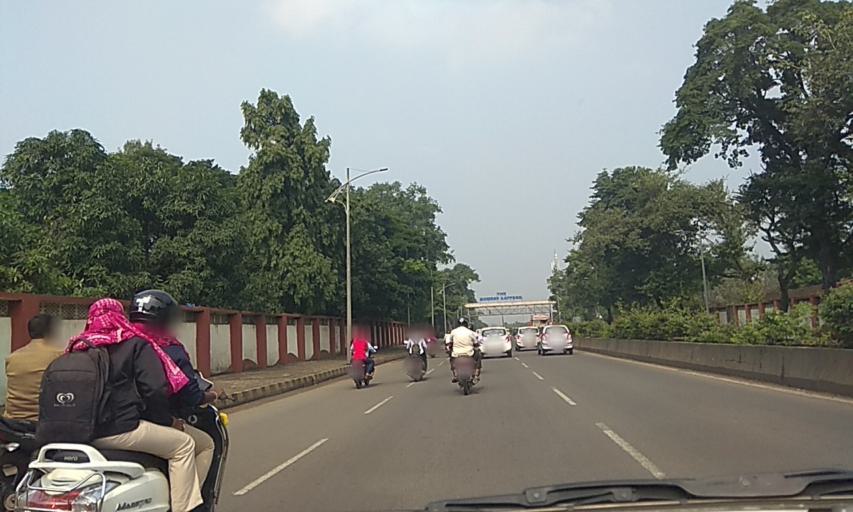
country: IN
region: Maharashtra
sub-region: Pune Division
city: Khadki
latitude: 18.5494
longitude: 73.8699
